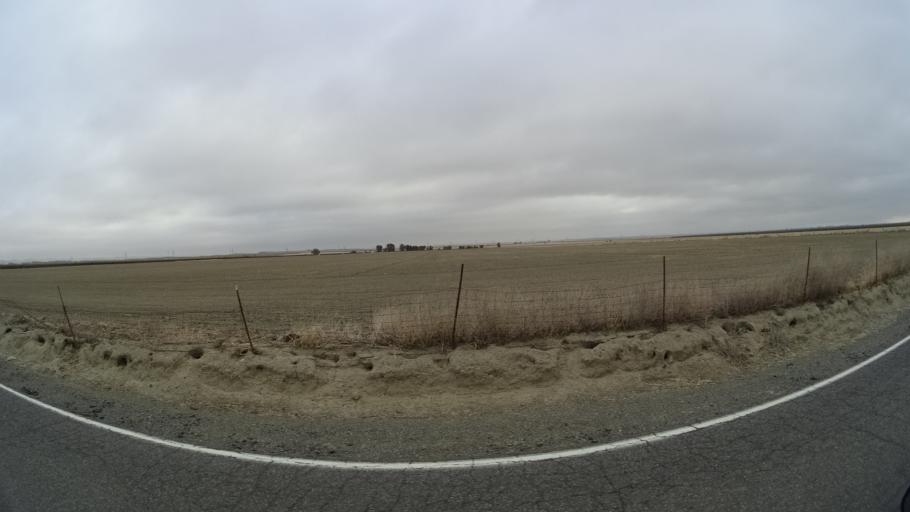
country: US
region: California
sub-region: Yolo County
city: Esparto
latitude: 38.7893
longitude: -122.0438
